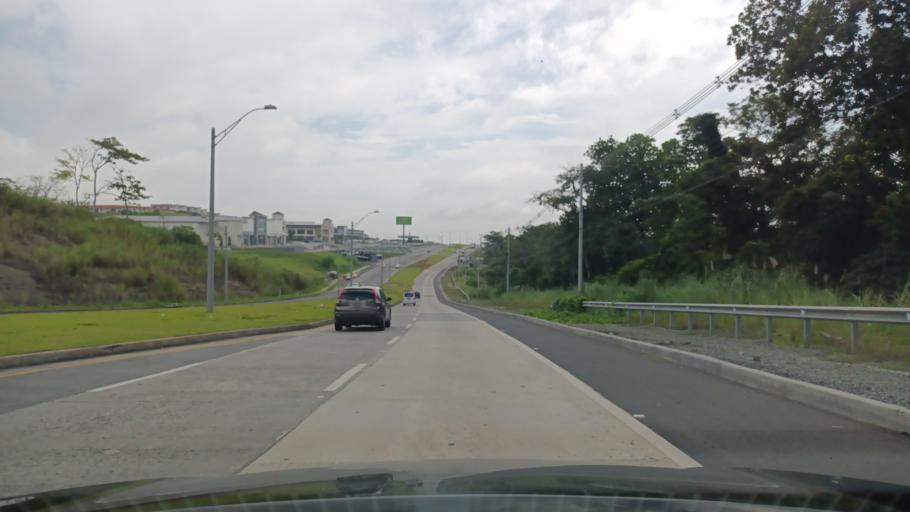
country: PA
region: Panama
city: Las Cumbres
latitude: 9.1033
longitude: -79.5255
